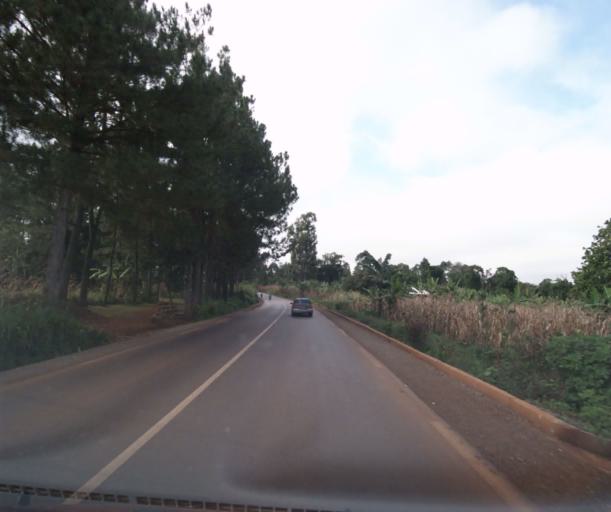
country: CM
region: West
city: Mbouda
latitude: 5.5899
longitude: 10.2954
